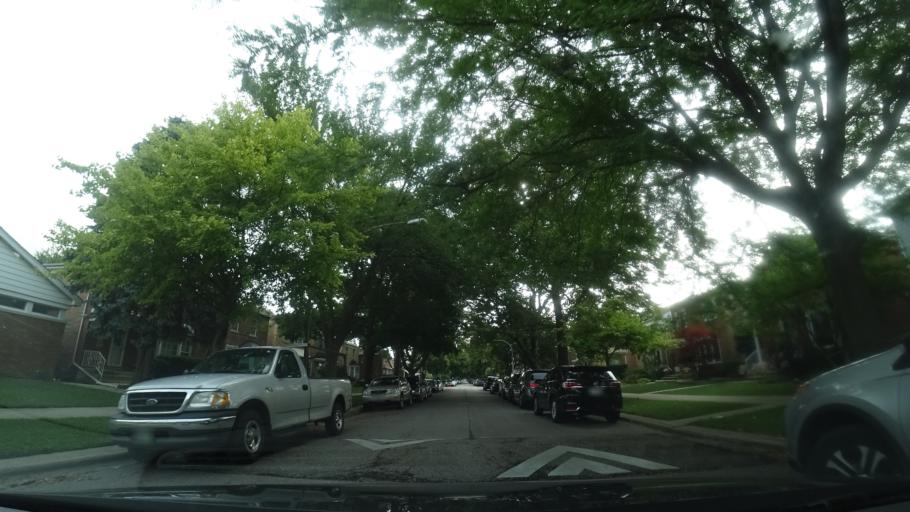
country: US
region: Illinois
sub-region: Cook County
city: Lincolnwood
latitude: 42.0165
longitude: -87.7053
